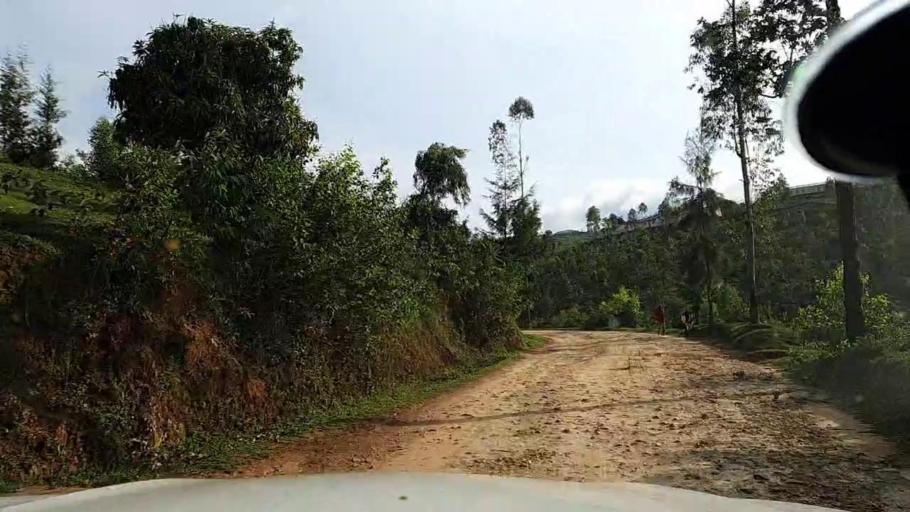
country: RW
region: Southern Province
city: Gitarama
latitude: -2.1735
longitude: 29.5557
